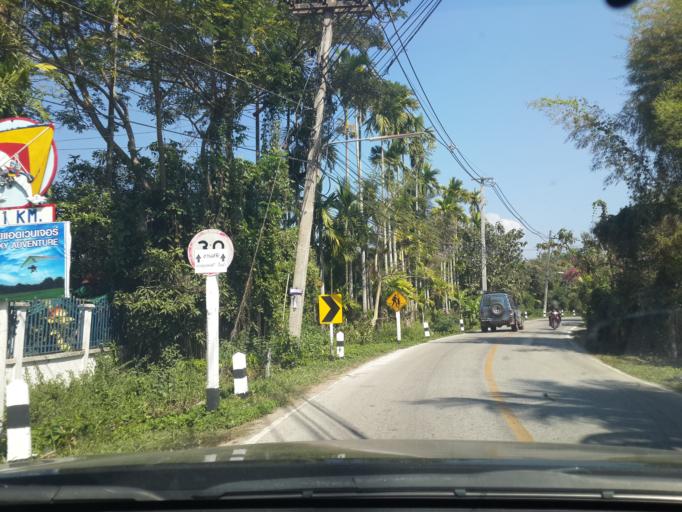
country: TH
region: Chiang Mai
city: San Sai
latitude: 18.8756
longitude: 99.0958
